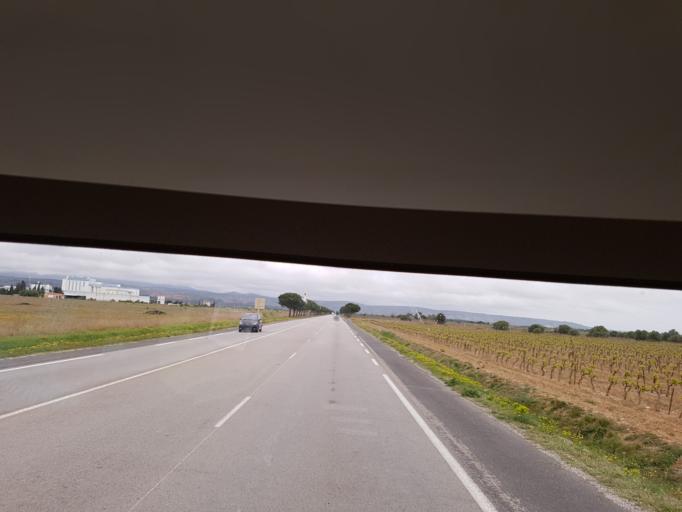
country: FR
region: Languedoc-Roussillon
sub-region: Departement des Pyrenees-Orientales
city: Salses-le-Chateau
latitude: 42.8021
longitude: 2.9106
